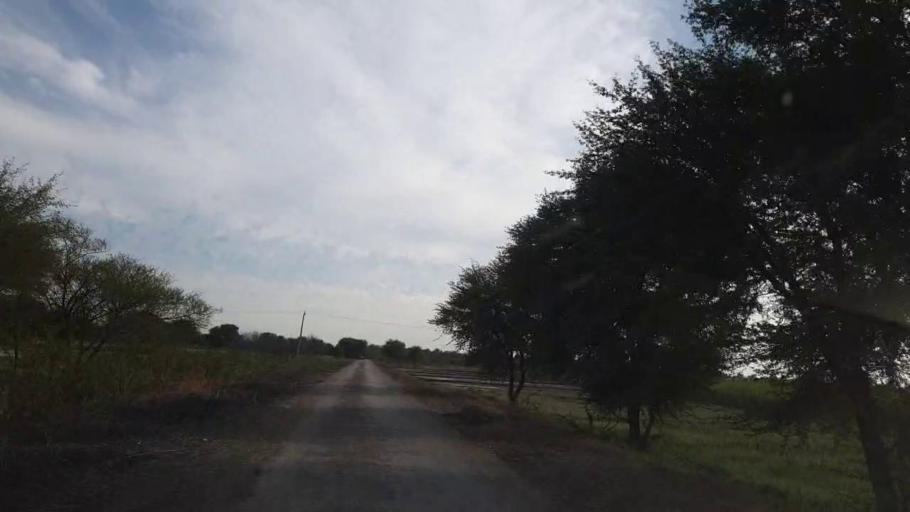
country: PK
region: Sindh
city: Pithoro
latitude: 25.6433
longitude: 69.3614
